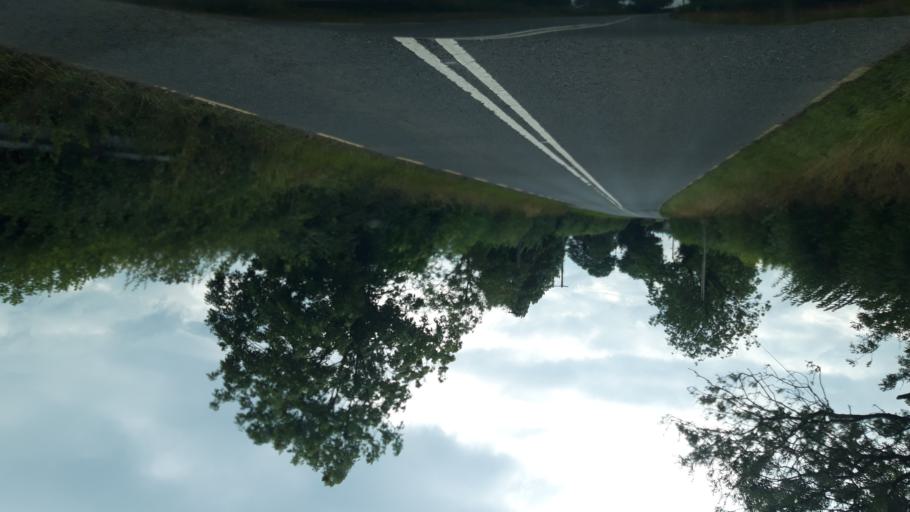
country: IE
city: Ballylinan
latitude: 52.8707
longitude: -7.0967
